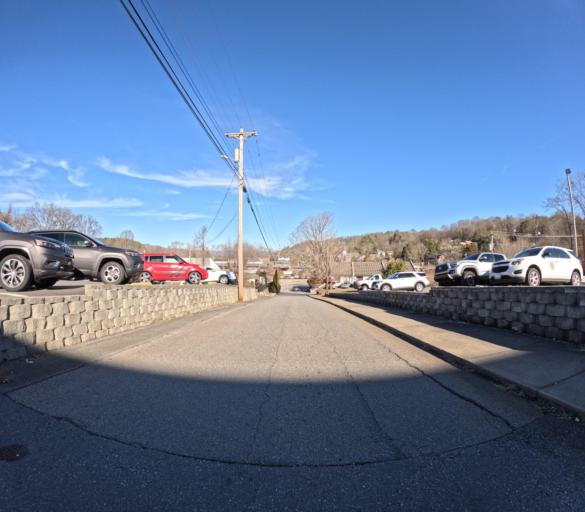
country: US
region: North Carolina
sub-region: Cherokee County
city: Murphy
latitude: 35.0875
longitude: -84.0325
